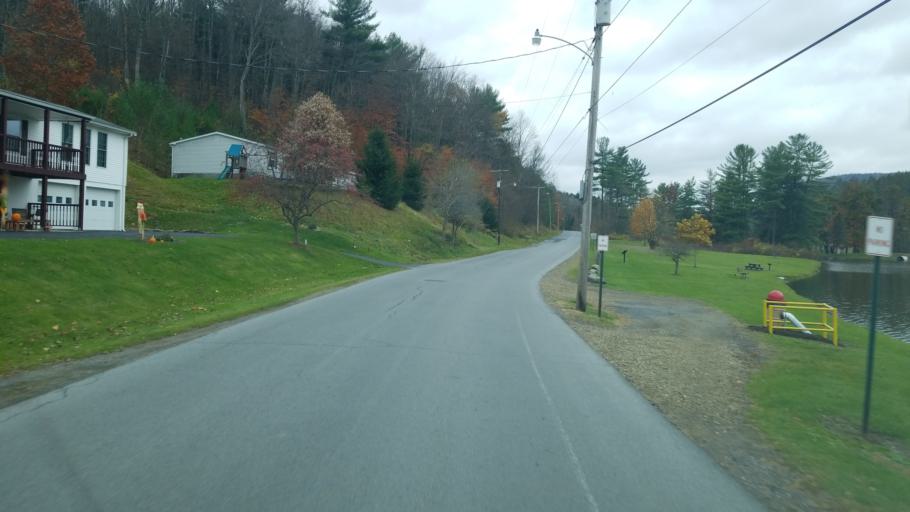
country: US
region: Pennsylvania
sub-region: McKean County
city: Smethport
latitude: 41.8057
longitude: -78.4456
